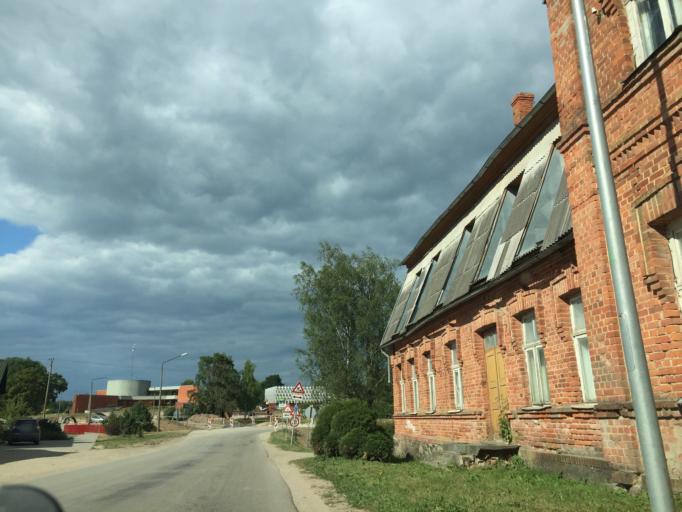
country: LV
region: Skriveri
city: Skriveri
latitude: 56.8447
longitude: 25.1545
